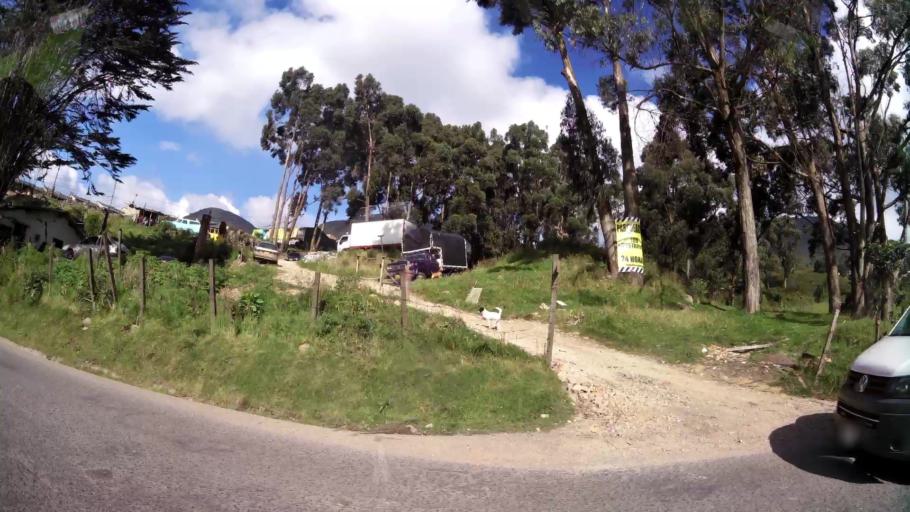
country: CO
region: Bogota D.C.
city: Bogota
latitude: 4.5327
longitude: -74.0850
